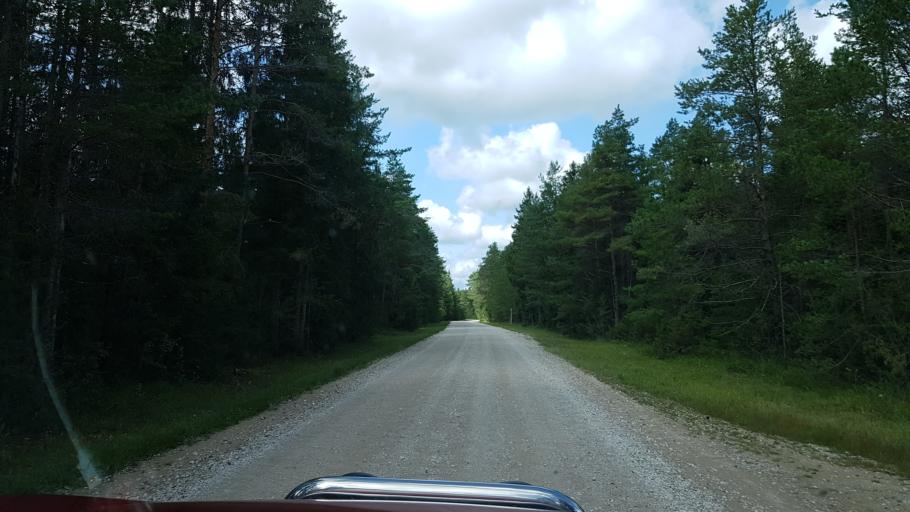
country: EE
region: Raplamaa
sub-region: Rapla vald
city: Rapla
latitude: 58.9561
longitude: 24.6586
